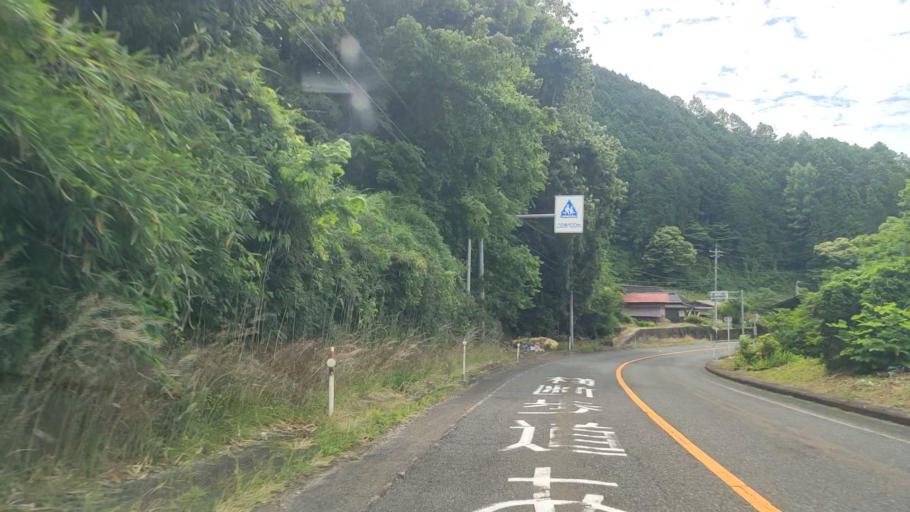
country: JP
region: Okayama
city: Niimi
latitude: 35.1562
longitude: 133.6273
